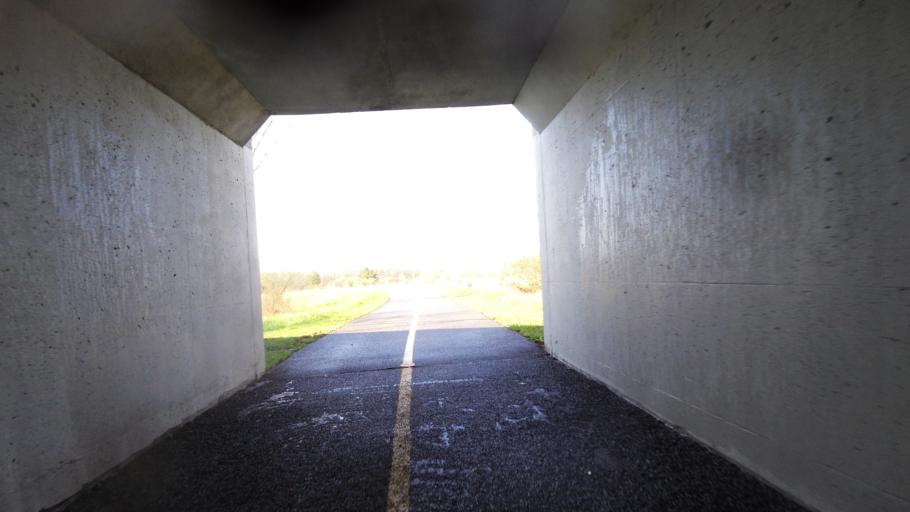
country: CA
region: Ontario
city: Bells Corners
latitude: 45.3436
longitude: -75.8800
